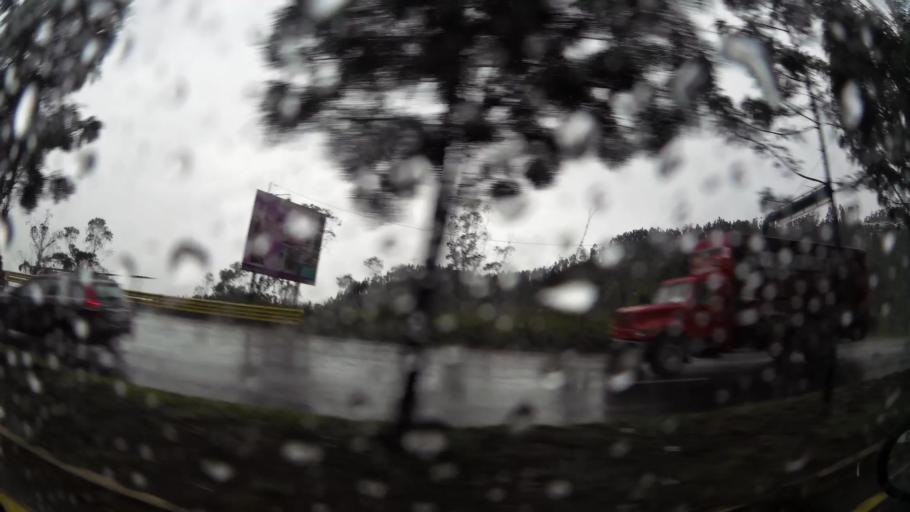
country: EC
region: Pichincha
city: Quito
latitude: -0.1497
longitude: -78.4501
